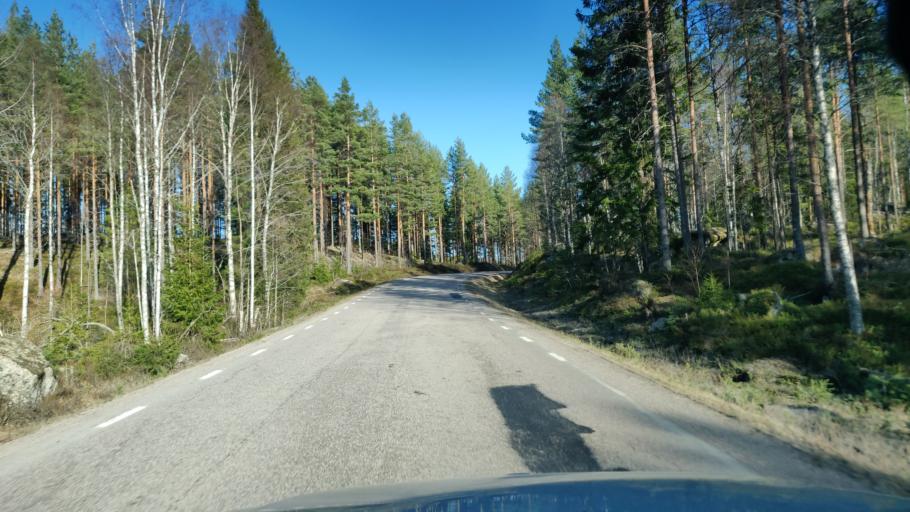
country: SE
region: Vaermland
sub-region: Hagfors Kommun
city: Ekshaerad
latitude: 59.9842
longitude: 13.3531
